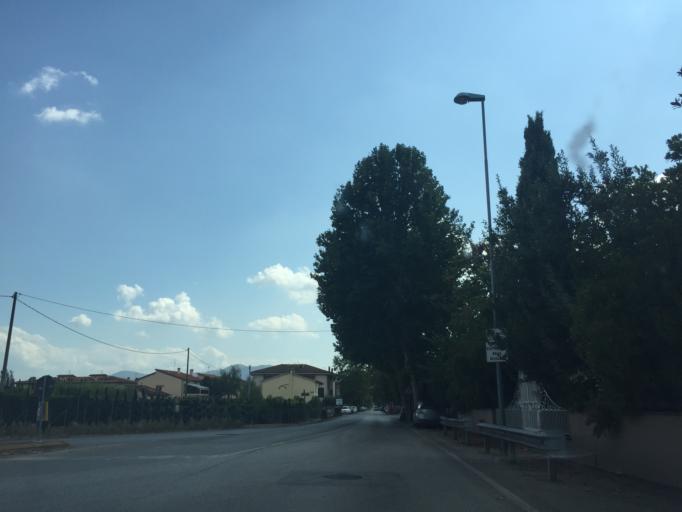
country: IT
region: Tuscany
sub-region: Provincia di Pistoia
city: Pistoia
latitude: 43.9008
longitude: 10.9179
